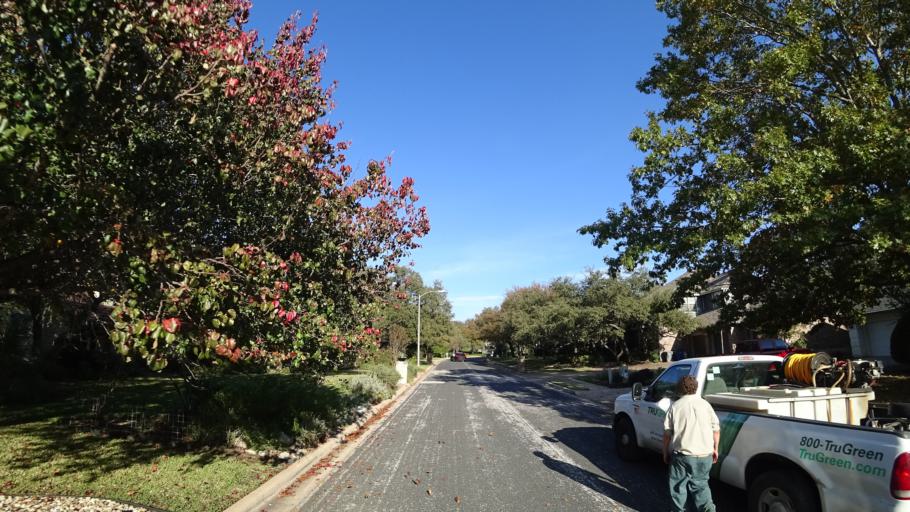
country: US
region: Texas
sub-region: Williamson County
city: Anderson Mill
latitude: 30.4305
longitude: -97.8119
